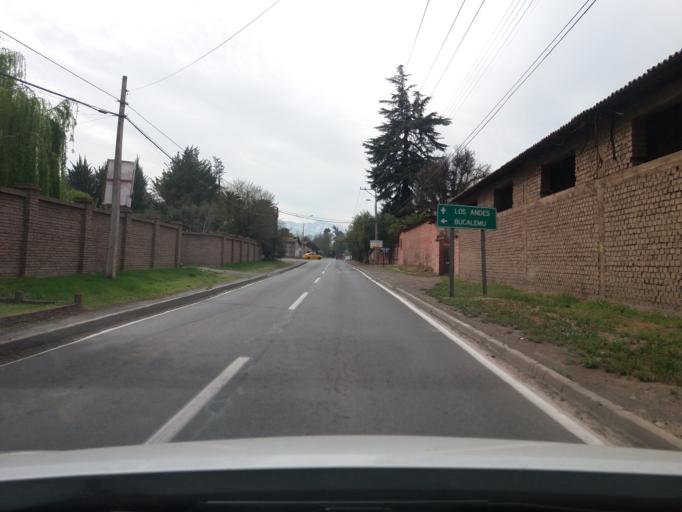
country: CL
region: Valparaiso
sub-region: Provincia de San Felipe
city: San Felipe
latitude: -32.8176
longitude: -70.6875
